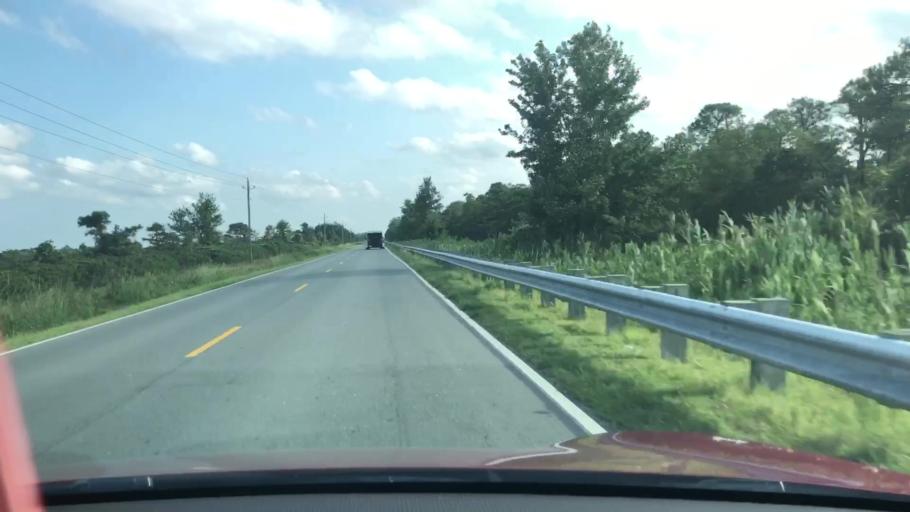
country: US
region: North Carolina
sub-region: Dare County
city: Wanchese
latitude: 35.7616
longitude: -75.7690
